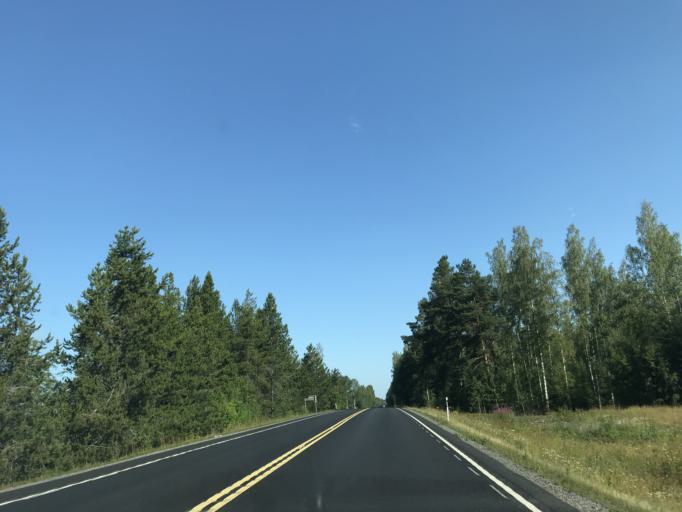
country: FI
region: Paijanne Tavastia
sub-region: Lahti
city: Lahti
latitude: 61.0702
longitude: 25.6679
